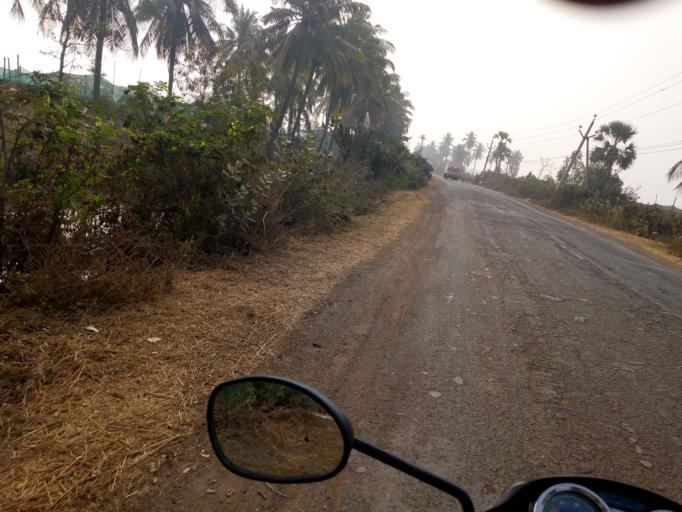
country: IN
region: Andhra Pradesh
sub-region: West Godavari
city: Pippara
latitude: 16.7355
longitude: 81.4191
